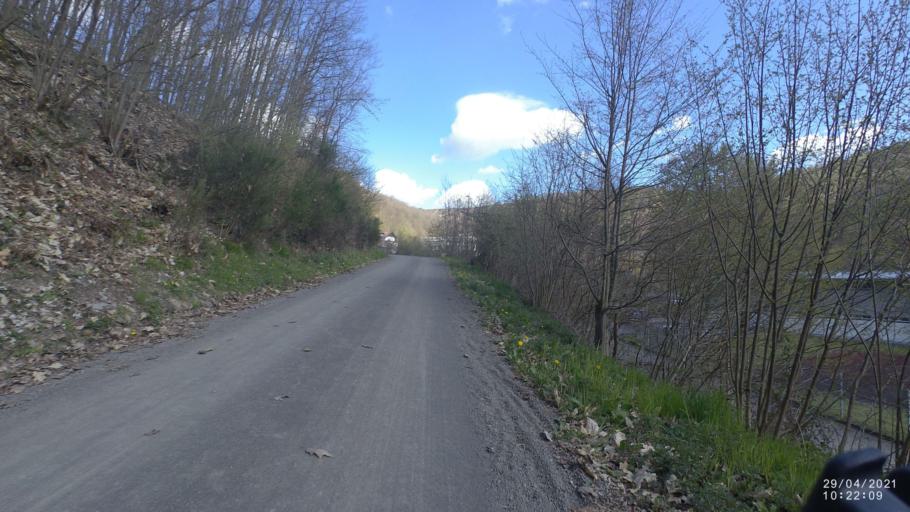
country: DE
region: Rheinland-Pfalz
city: Mayen
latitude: 50.3366
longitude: 7.2114
